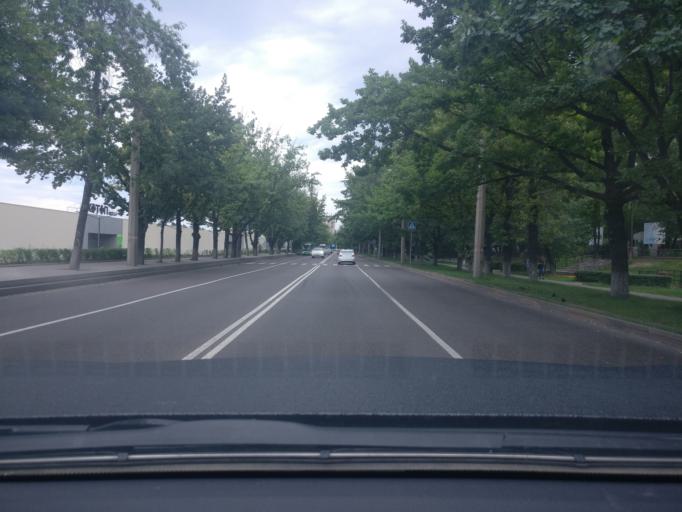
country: KZ
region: Almaty Qalasy
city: Almaty
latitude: 43.2373
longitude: 76.8548
